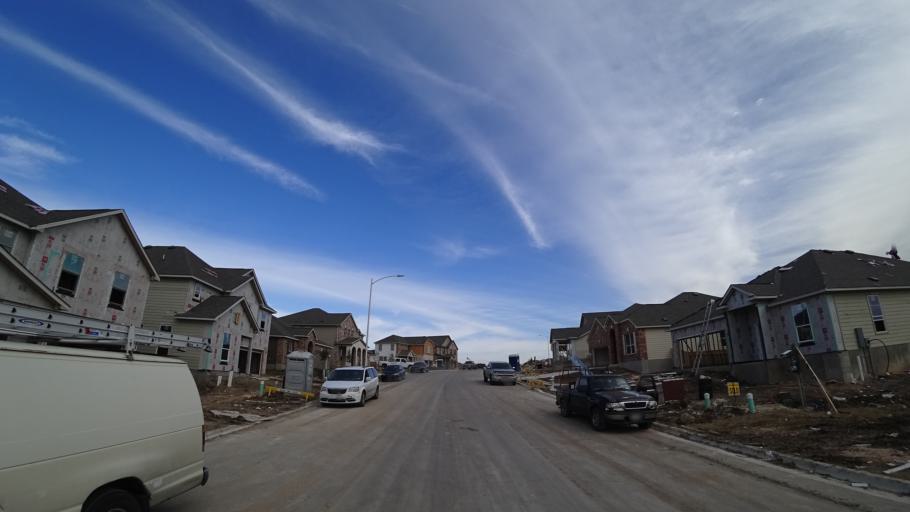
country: US
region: Texas
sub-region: Travis County
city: Onion Creek
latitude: 30.1605
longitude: -97.7336
